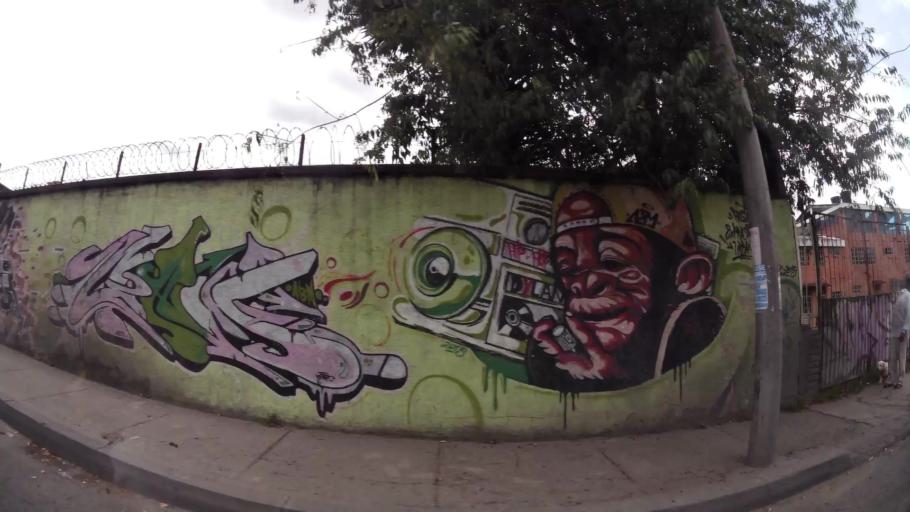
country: CO
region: Cundinamarca
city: Funza
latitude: 4.7102
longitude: -74.1203
